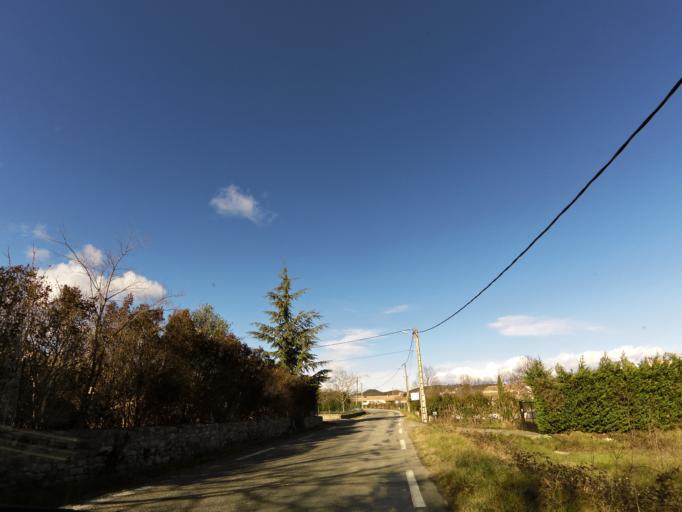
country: FR
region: Languedoc-Roussillon
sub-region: Departement du Gard
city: Sauve
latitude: 43.9862
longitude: 3.9518
